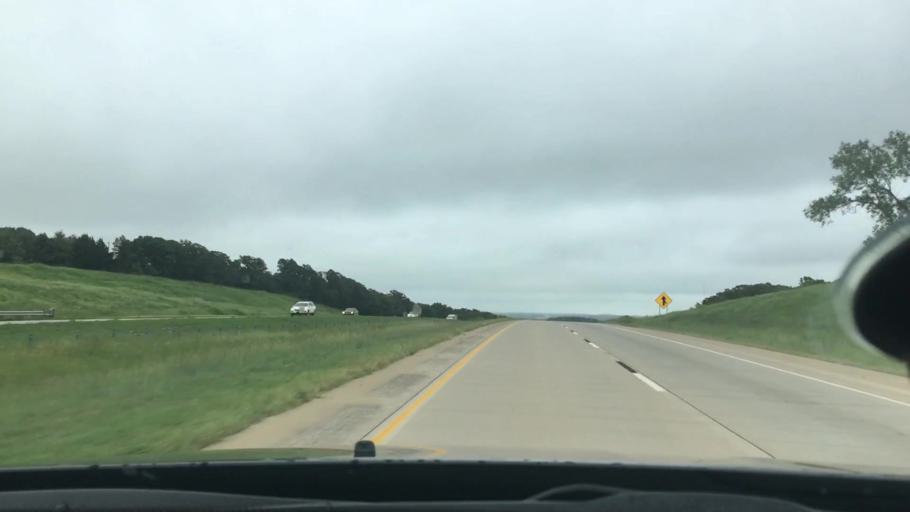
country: US
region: Oklahoma
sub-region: Okfuskee County
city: Okemah
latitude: 35.4303
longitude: -96.1932
